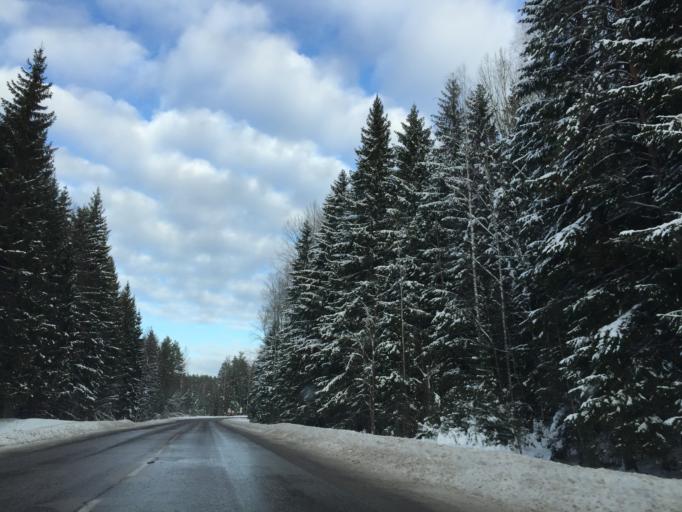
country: LV
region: Ropazu
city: Ropazi
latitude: 57.0086
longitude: 24.6777
